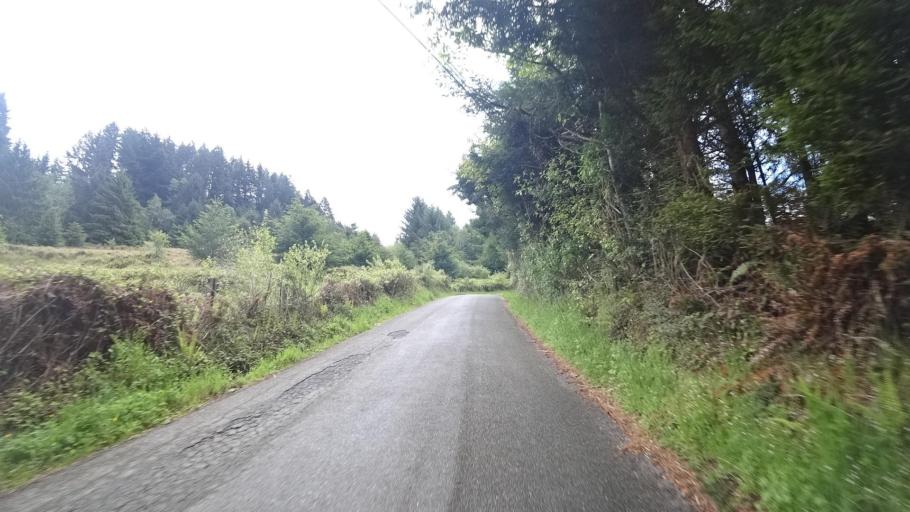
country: US
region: California
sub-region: Humboldt County
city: Bayside
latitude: 40.8431
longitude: -124.0244
